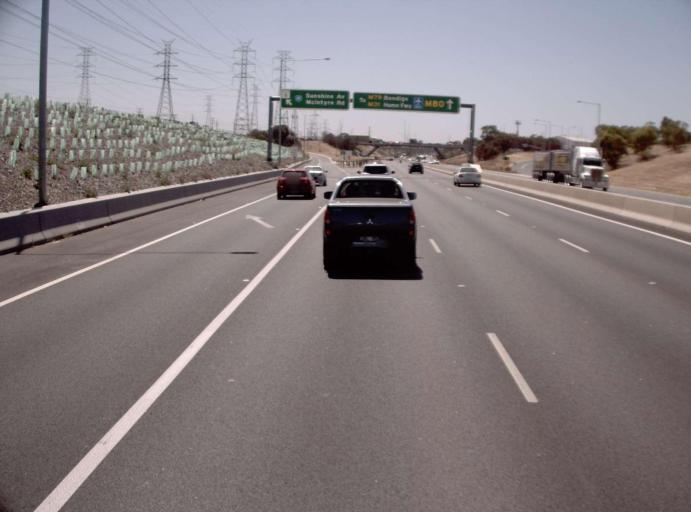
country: AU
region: Victoria
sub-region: Brimbank
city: Albion
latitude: -37.7535
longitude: 144.8280
